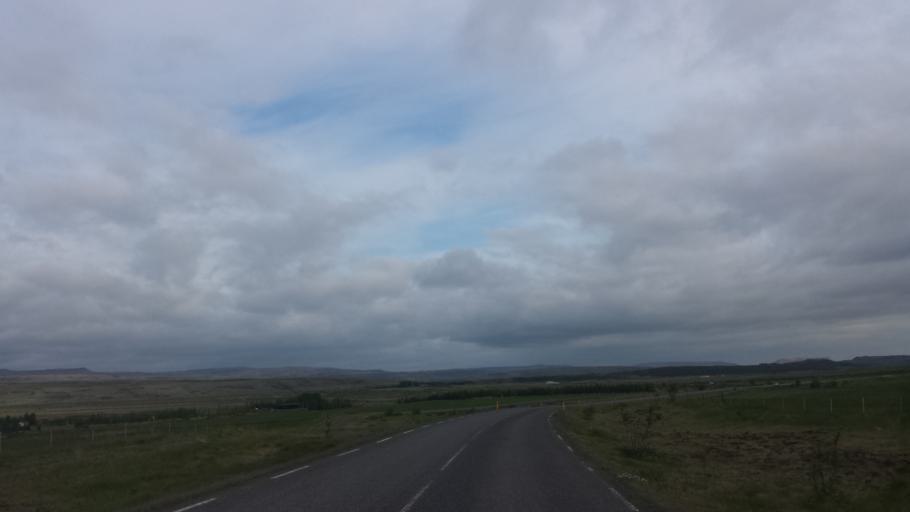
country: IS
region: South
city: Selfoss
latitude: 64.2534
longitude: -20.3227
